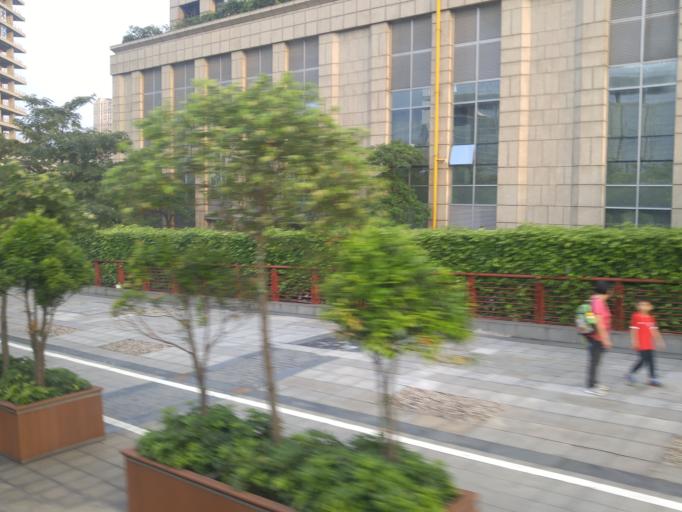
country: CN
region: Guangdong
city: Foshan
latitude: 23.0605
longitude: 113.1422
